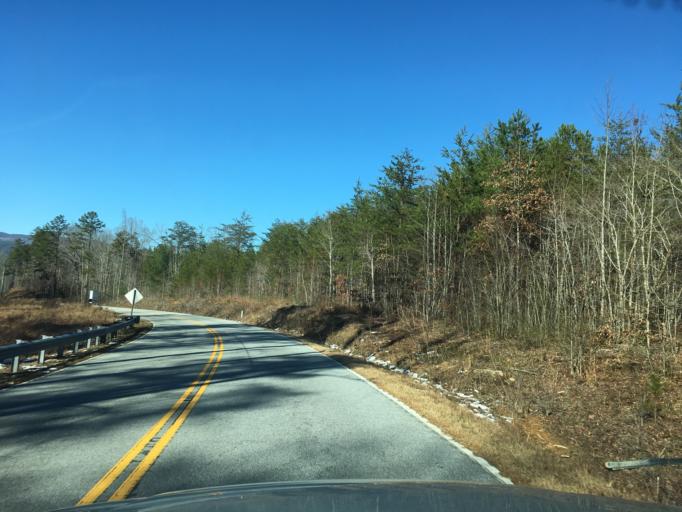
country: US
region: South Carolina
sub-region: Oconee County
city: Walhalla
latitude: 34.9237
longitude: -82.9833
